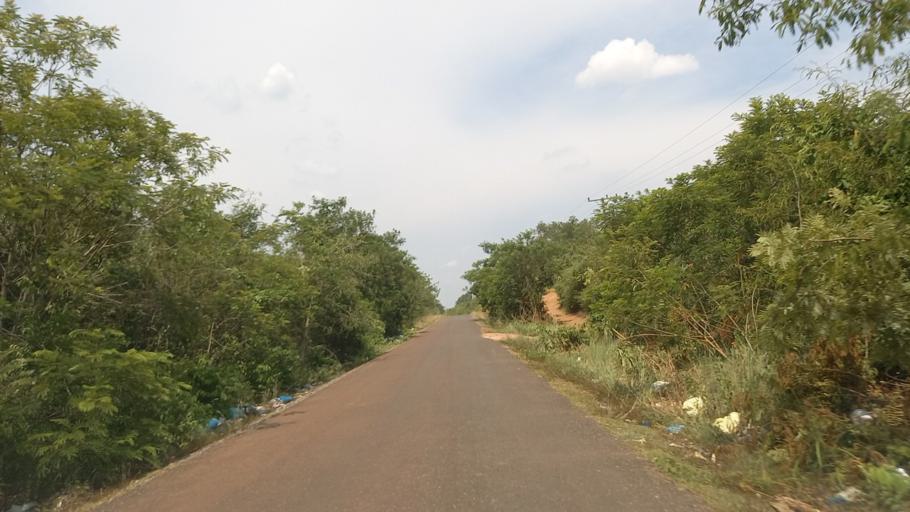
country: LA
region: Bolikhamxai
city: Muang Pakxan
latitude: 18.4288
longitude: 103.7297
